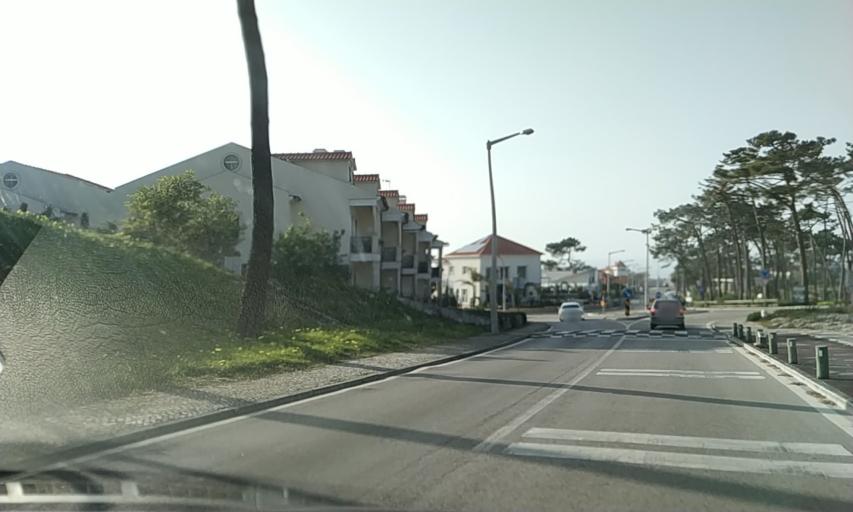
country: PT
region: Leiria
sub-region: Alcobaca
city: Pataias
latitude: 39.7566
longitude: -9.0269
